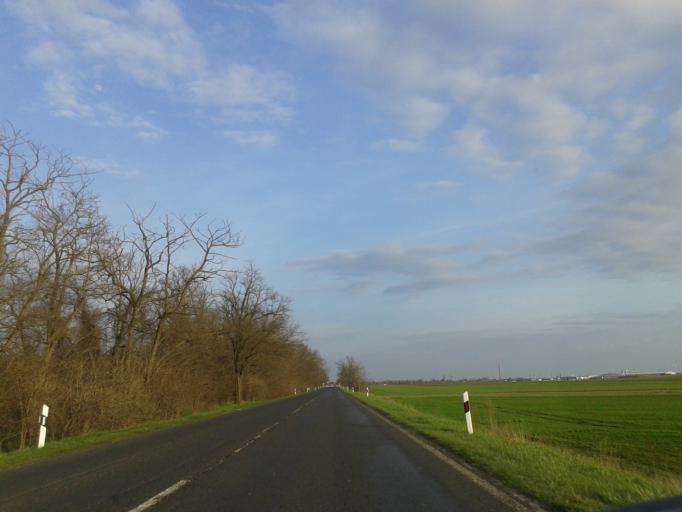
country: HU
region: Komarom-Esztergom
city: Acs
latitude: 47.7324
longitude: 17.9789
